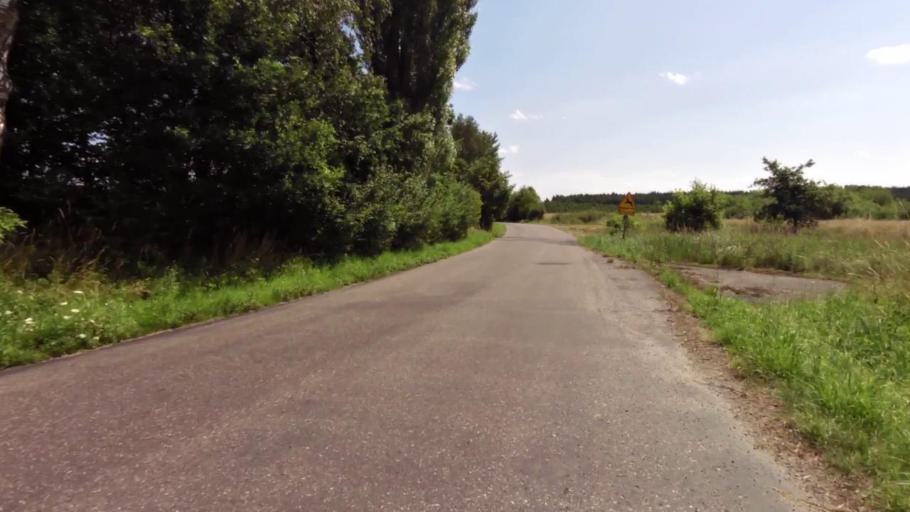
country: PL
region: West Pomeranian Voivodeship
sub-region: Powiat stargardzki
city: Dobrzany
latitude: 53.3838
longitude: 15.3728
